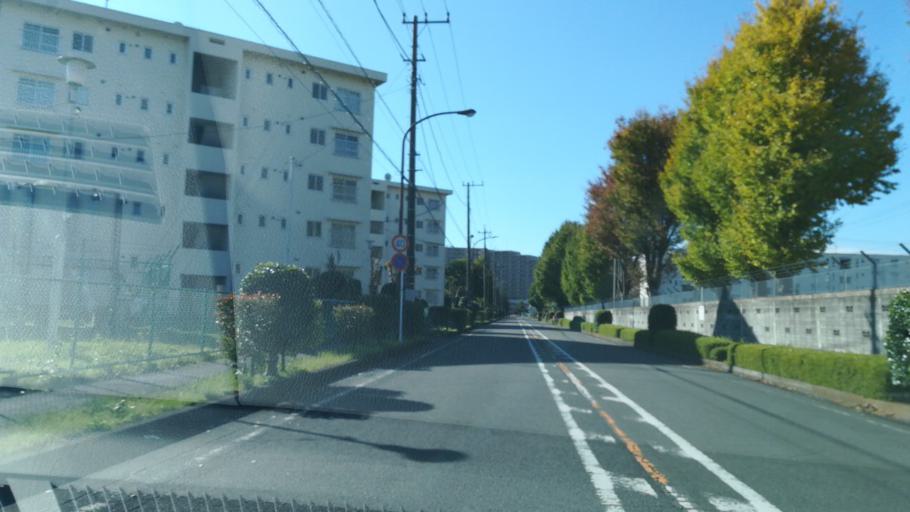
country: JP
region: Tokyo
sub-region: Machida-shi
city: Machida
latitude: 35.5777
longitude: 139.3893
